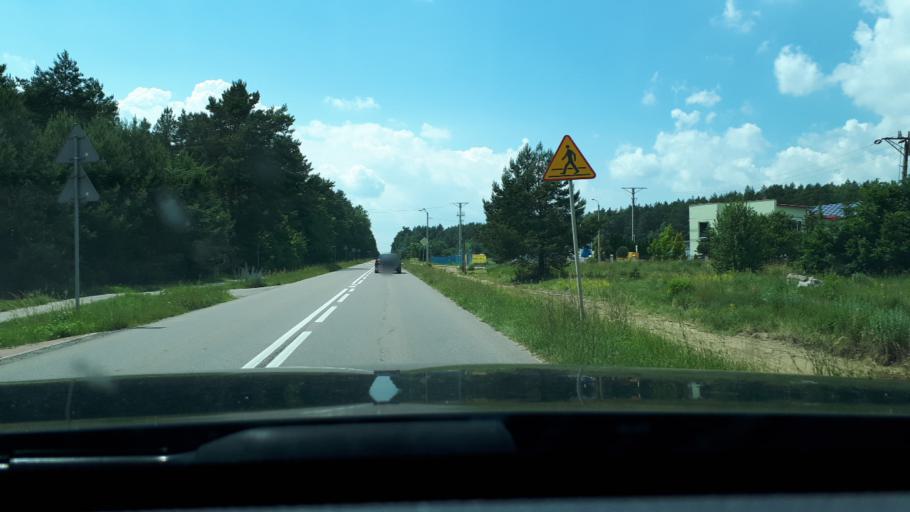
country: PL
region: Podlasie
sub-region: Powiat bialostocki
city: Choroszcz
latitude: 53.1317
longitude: 23.0466
